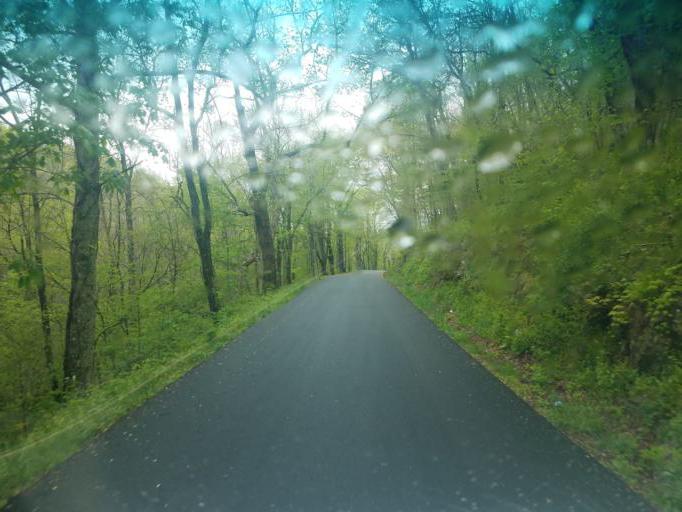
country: US
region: Virginia
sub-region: Smyth County
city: Marion
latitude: 36.9230
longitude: -81.5560
